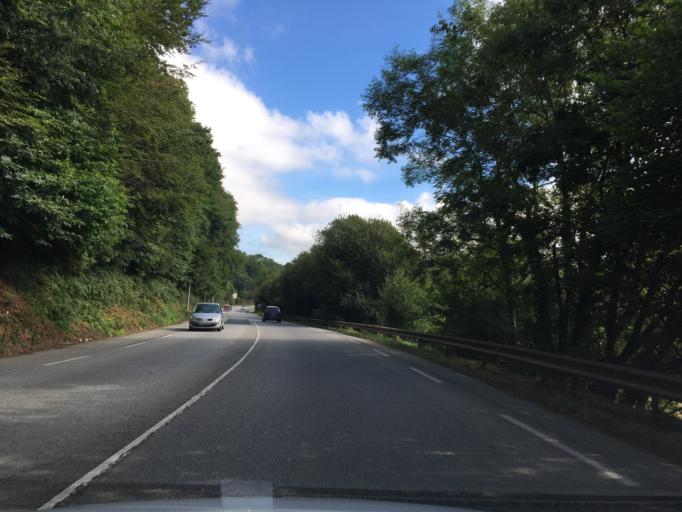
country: FR
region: Brittany
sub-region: Departement du Finistere
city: Quimper
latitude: 48.0058
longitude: -4.0832
